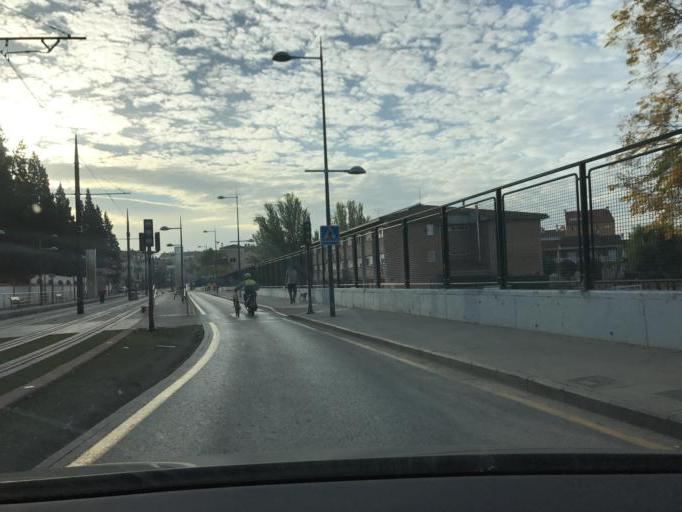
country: ES
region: Andalusia
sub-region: Provincia de Granada
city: Maracena
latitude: 37.2115
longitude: -3.6349
